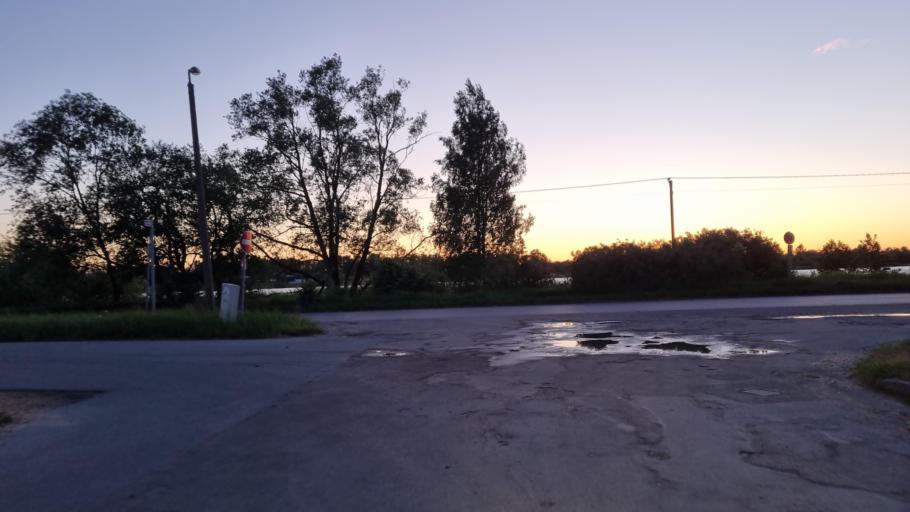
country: LV
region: Riga
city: Daugavgriva
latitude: 57.0248
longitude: 24.0254
